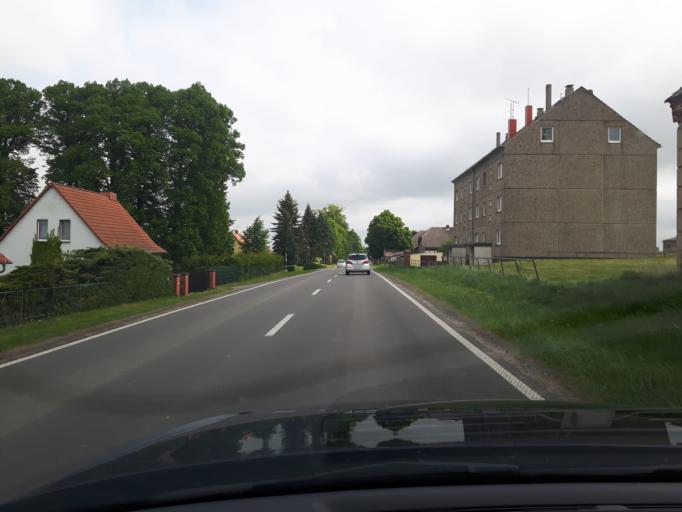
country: DE
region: Mecklenburg-Vorpommern
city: Gross Wokern
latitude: 53.6426
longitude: 12.4871
